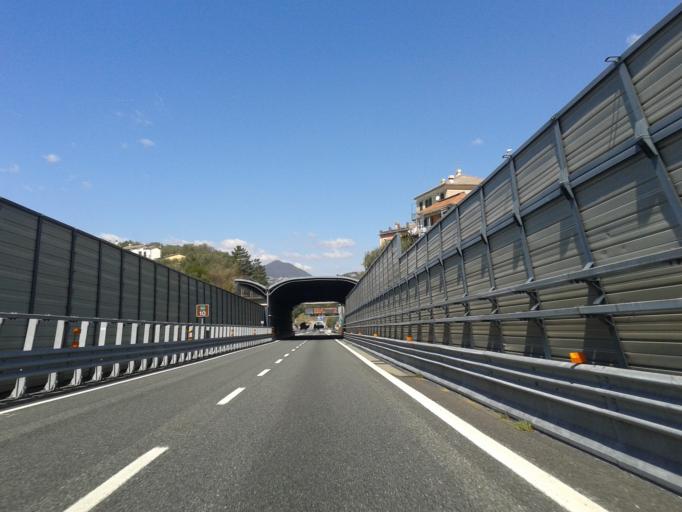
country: IT
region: Liguria
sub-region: Provincia di Genova
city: Lavagna
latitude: 44.3094
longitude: 9.3631
